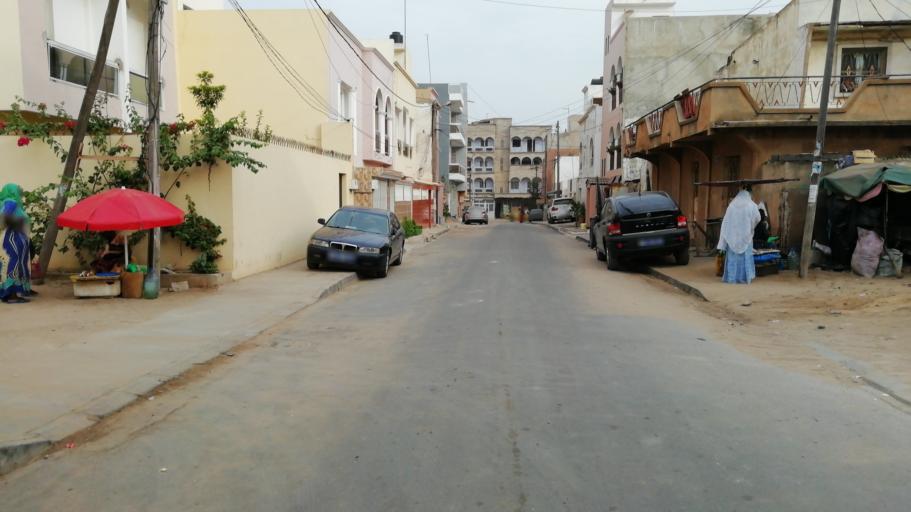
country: SN
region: Dakar
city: Grand Dakar
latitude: 14.7580
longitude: -17.4482
